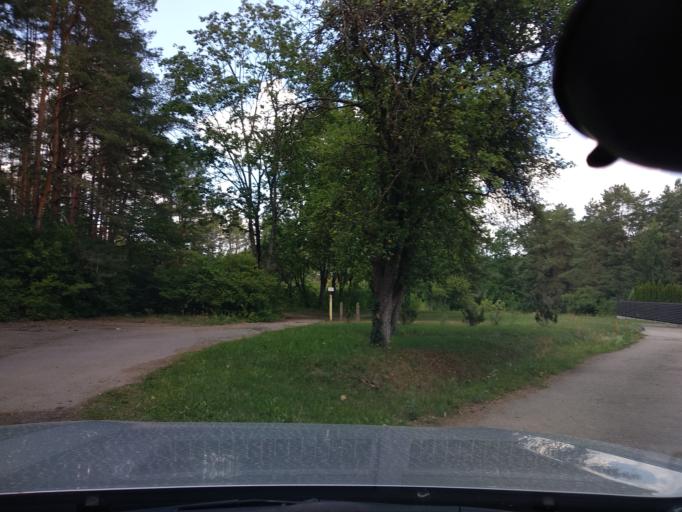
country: LT
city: Grigiskes
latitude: 54.6821
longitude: 25.0788
